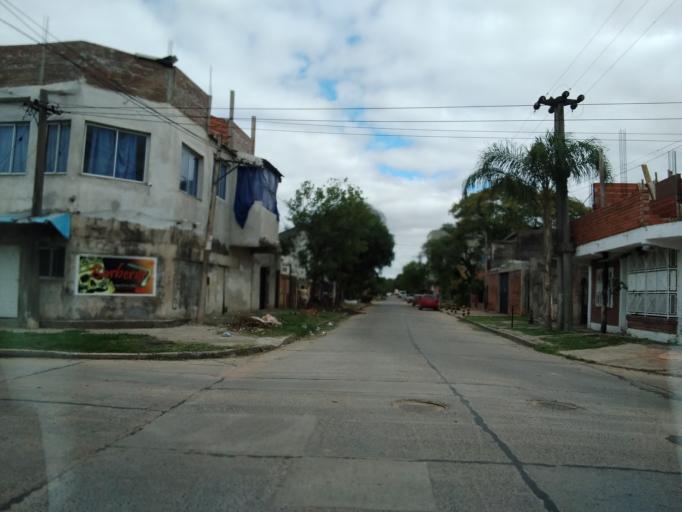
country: AR
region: Corrientes
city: Corrientes
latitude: -27.4761
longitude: -58.8107
